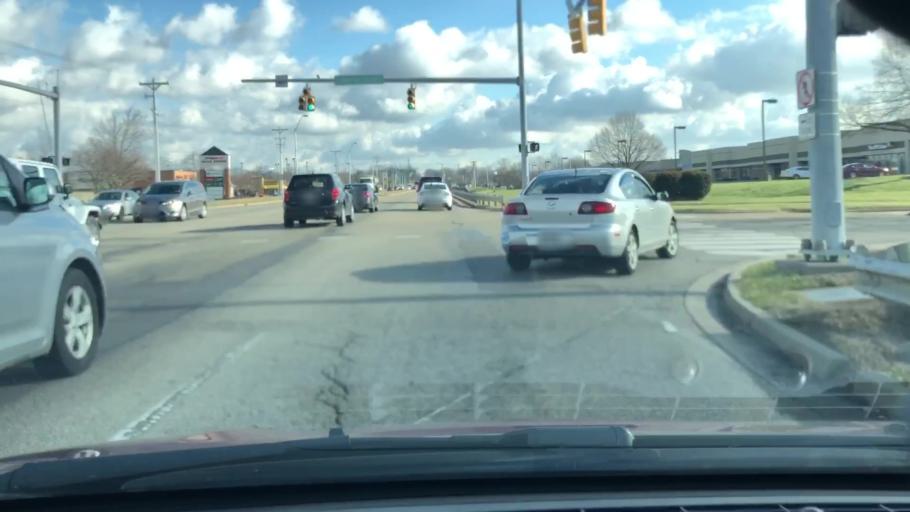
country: US
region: Ohio
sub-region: Greene County
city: Fairborn
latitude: 39.7833
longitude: -83.9977
